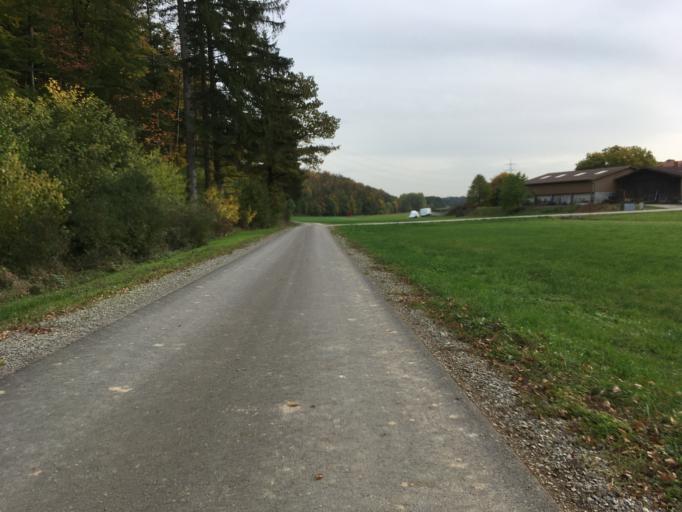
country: DE
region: Baden-Wuerttemberg
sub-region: Karlsruhe Region
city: Buchen
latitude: 49.4908
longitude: 9.3413
